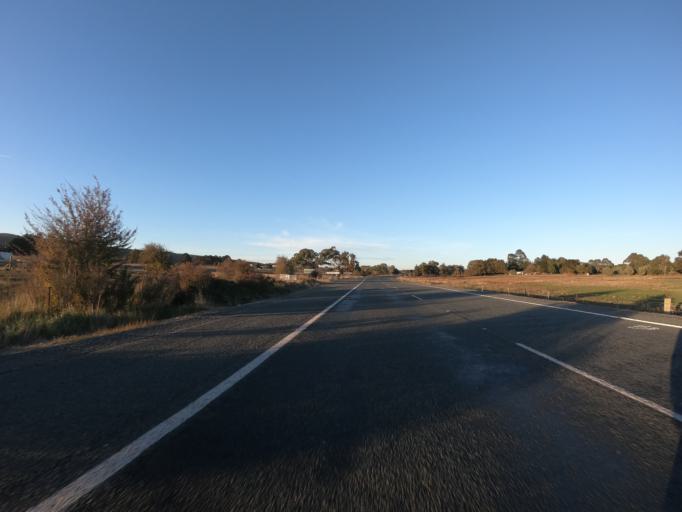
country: AU
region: New South Wales
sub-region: Goulburn Mulwaree
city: Goulburn
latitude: -34.8248
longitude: 149.5983
